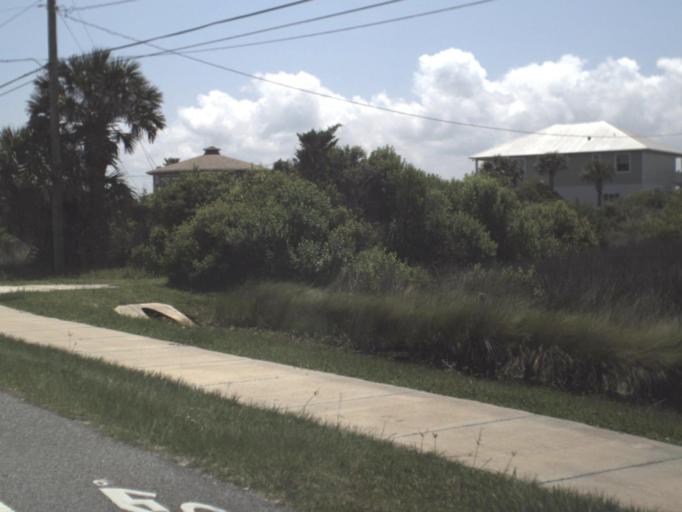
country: US
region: Florida
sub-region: Saint Johns County
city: Butler Beach
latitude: 29.7469
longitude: -81.2453
